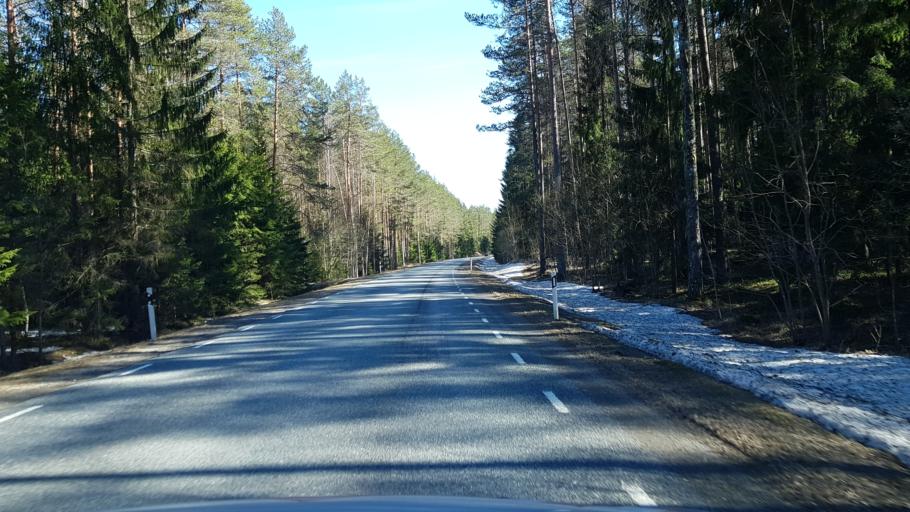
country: EE
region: Laeaene-Virumaa
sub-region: Vinni vald
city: Vinni
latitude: 59.2627
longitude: 26.6789
